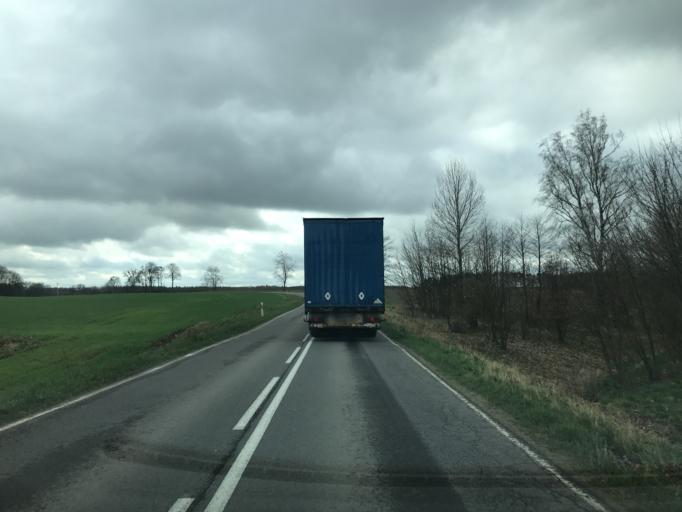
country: PL
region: Warmian-Masurian Voivodeship
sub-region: Powiat ostrodzki
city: Gierzwald
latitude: 53.5118
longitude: 20.1855
